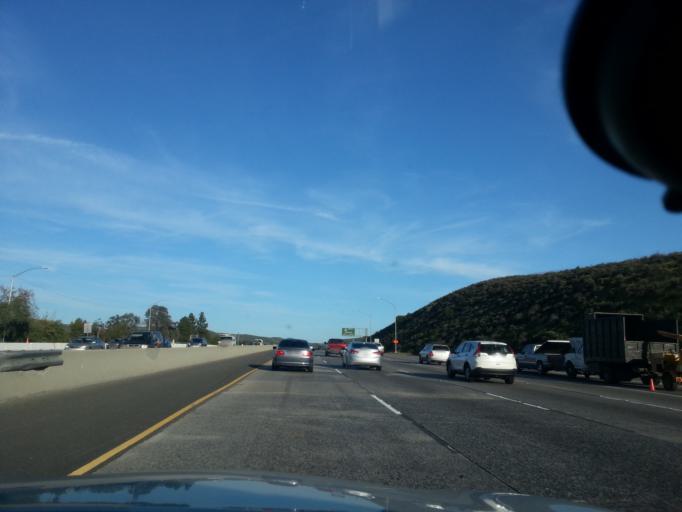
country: US
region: California
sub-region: Ventura County
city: Thousand Oaks
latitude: 34.1771
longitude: -118.8740
